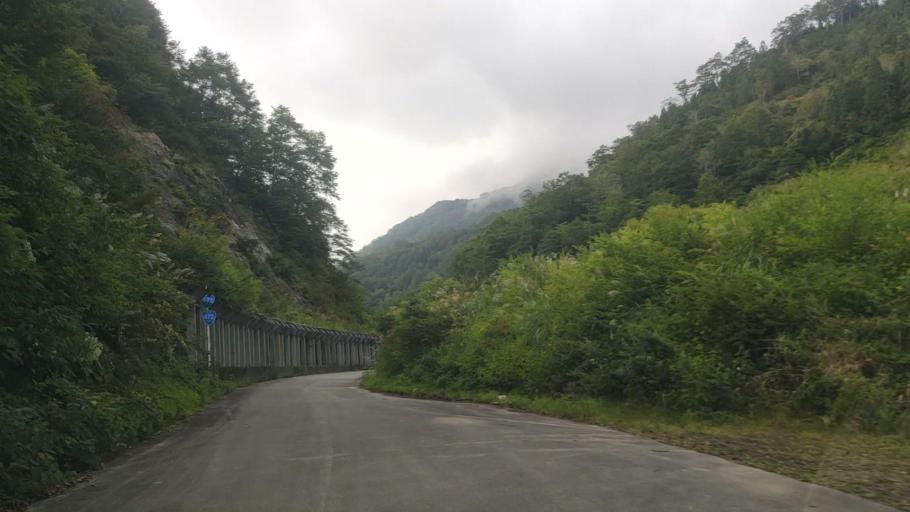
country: JP
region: Toyama
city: Yatsuomachi-higashikumisaka
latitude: 36.3837
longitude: 137.0854
